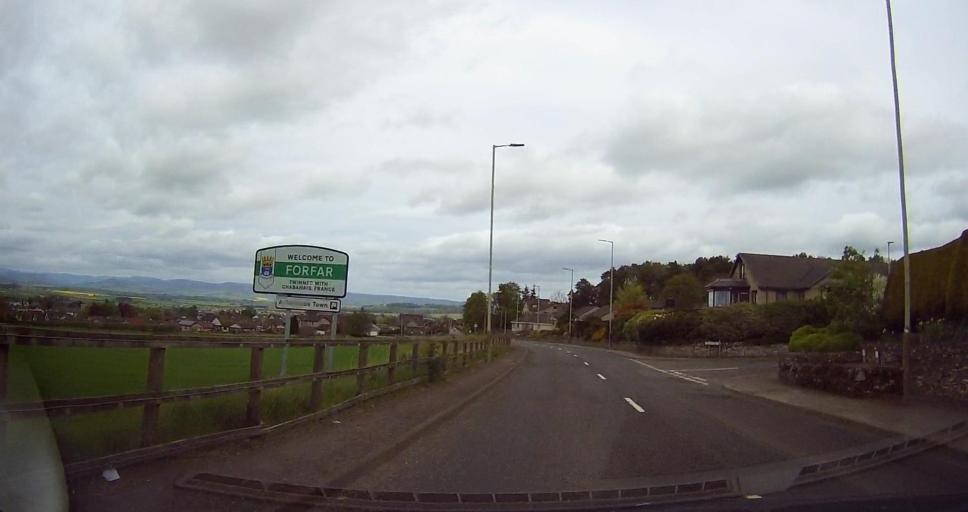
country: GB
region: Scotland
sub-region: Angus
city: Forfar
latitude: 56.6292
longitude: -2.8972
